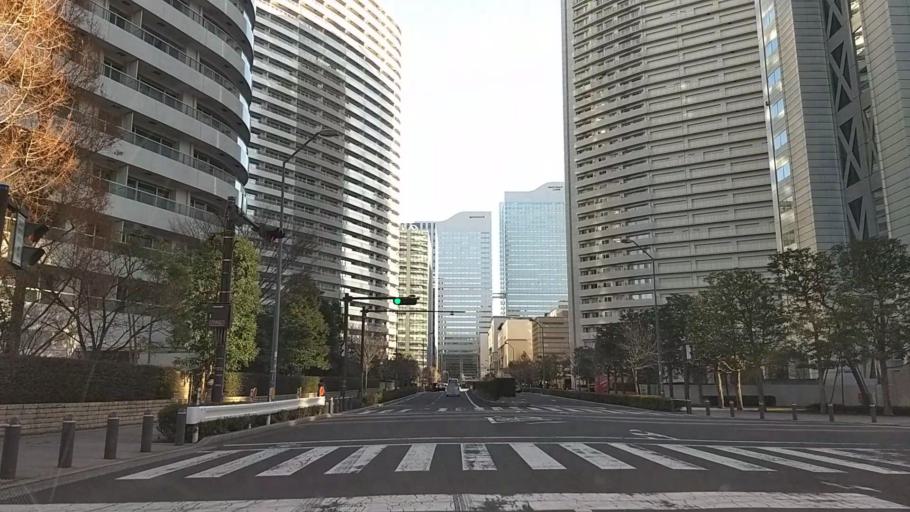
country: JP
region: Kanagawa
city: Yokohama
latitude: 35.4607
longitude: 139.6302
